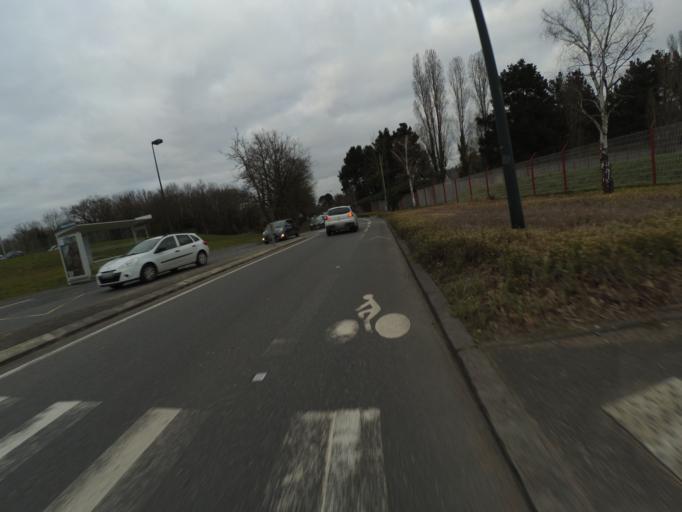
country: FR
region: Pays de la Loire
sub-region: Departement de la Loire-Atlantique
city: Sainte-Luce-sur-Loire
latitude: 47.2669
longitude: -1.5031
